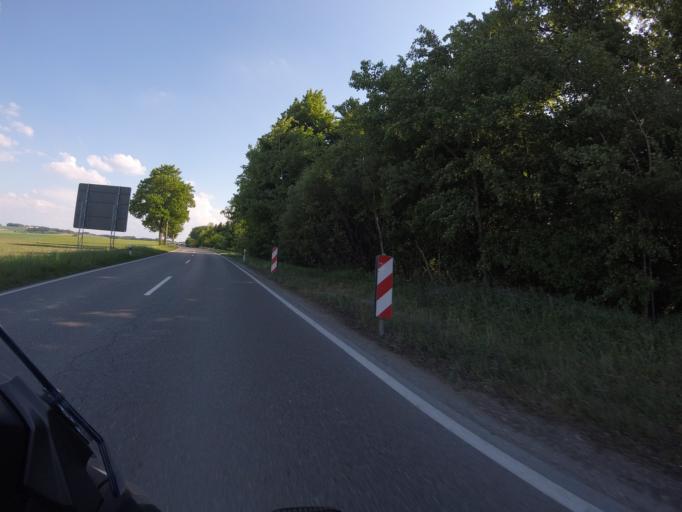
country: DE
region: Bavaria
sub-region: Upper Bavaria
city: Fahrenzhausen
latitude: 48.3353
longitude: 11.5711
